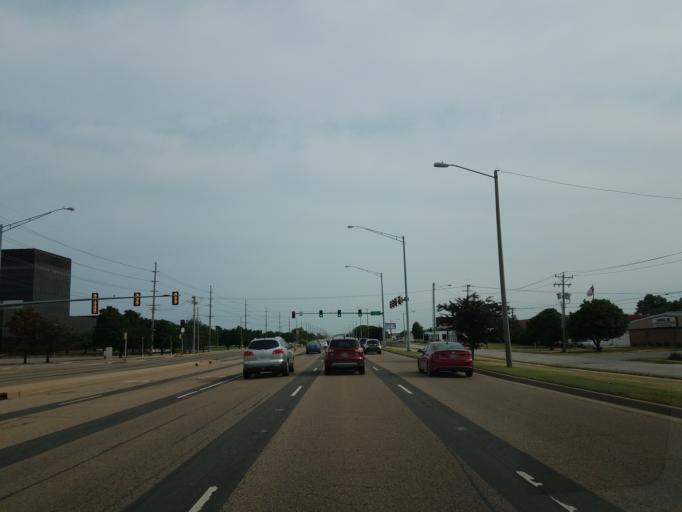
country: US
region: Illinois
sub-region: McLean County
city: Bloomington
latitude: 40.4747
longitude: -88.9524
